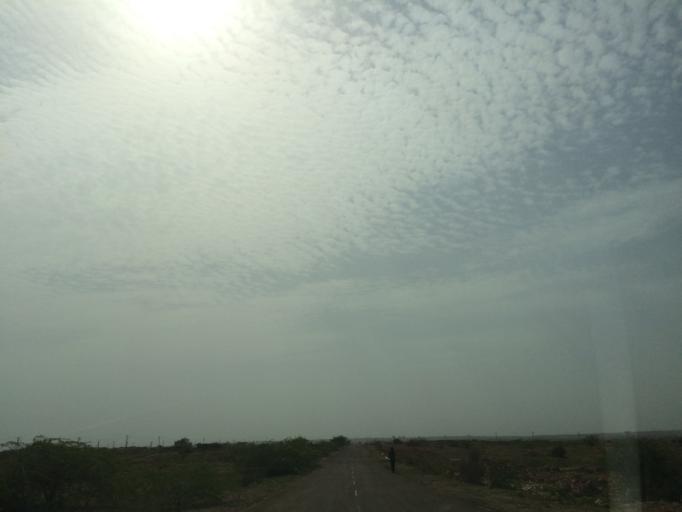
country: IN
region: Rajasthan
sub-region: Jaisalmer
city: Jaisalmer
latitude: 26.8736
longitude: 70.8992
